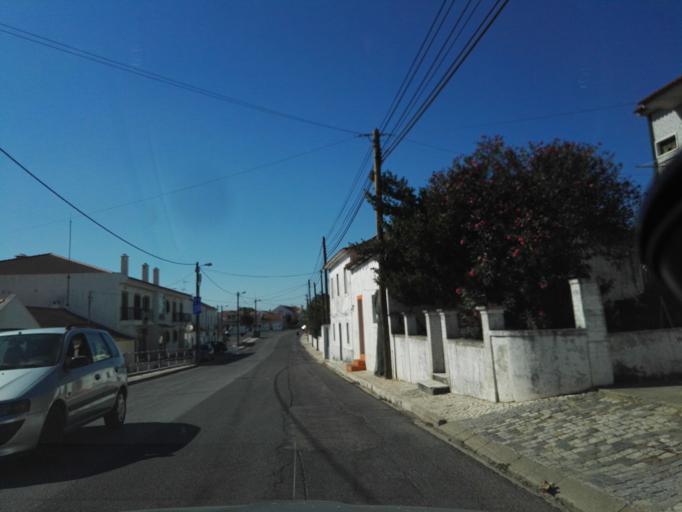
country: PT
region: Santarem
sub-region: Benavente
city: Poceirao
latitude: 38.8591
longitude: -8.7421
